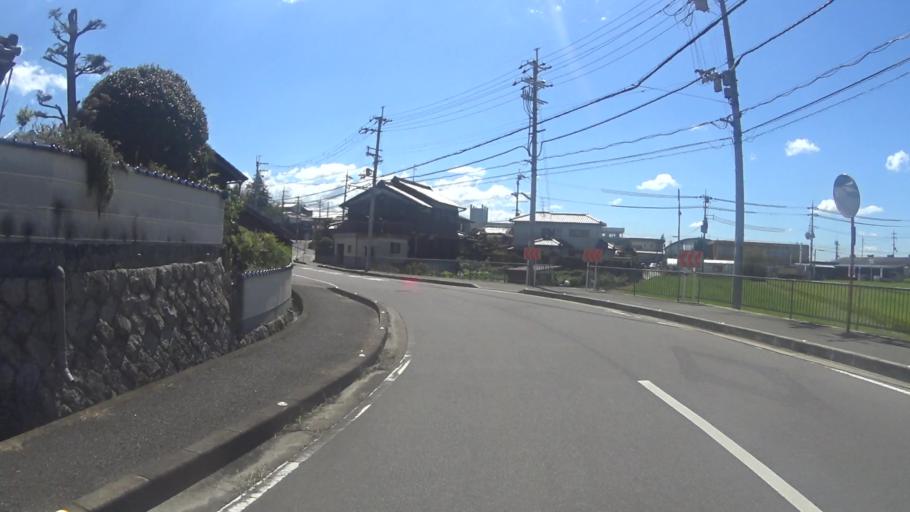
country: JP
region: Nara
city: Nara-shi
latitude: 34.7594
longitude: 135.8161
